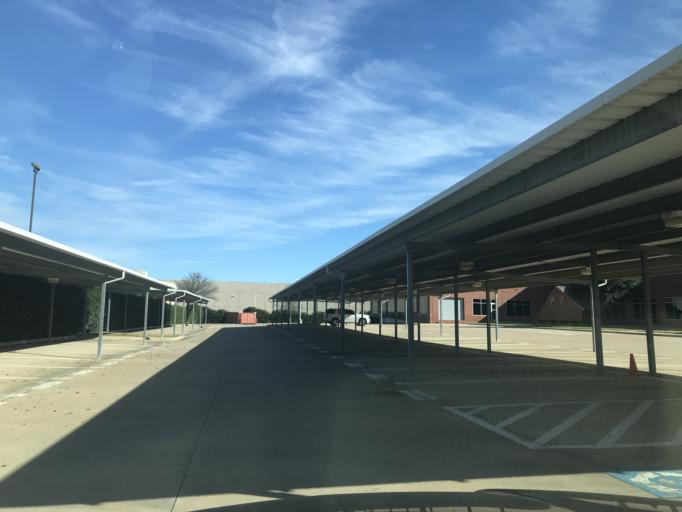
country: US
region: Texas
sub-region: Tarrant County
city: Haltom City
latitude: 32.8186
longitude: -97.3114
